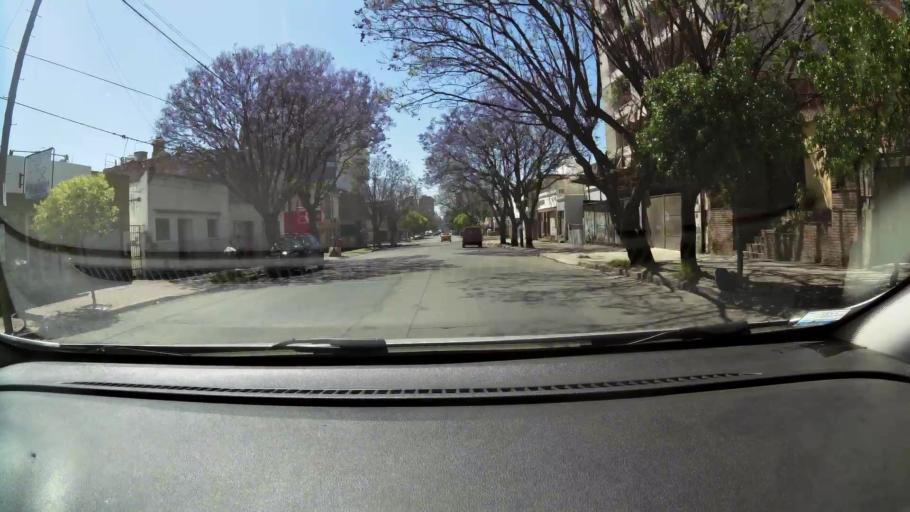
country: AR
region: Cordoba
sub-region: Departamento de Capital
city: Cordoba
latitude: -31.4223
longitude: -64.2053
